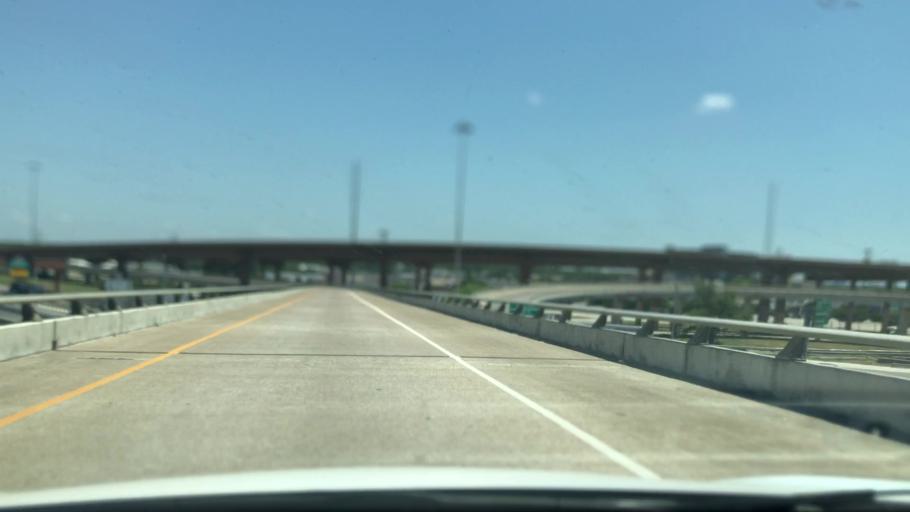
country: US
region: Texas
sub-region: Dallas County
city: Farmers Branch
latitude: 32.9089
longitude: -96.8985
